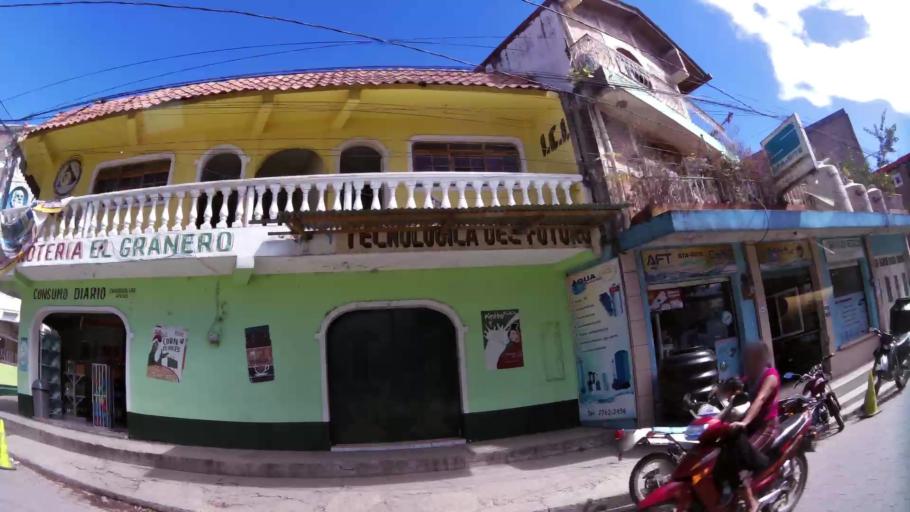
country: GT
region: Solola
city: Panajachel
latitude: 14.7430
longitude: -91.1531
